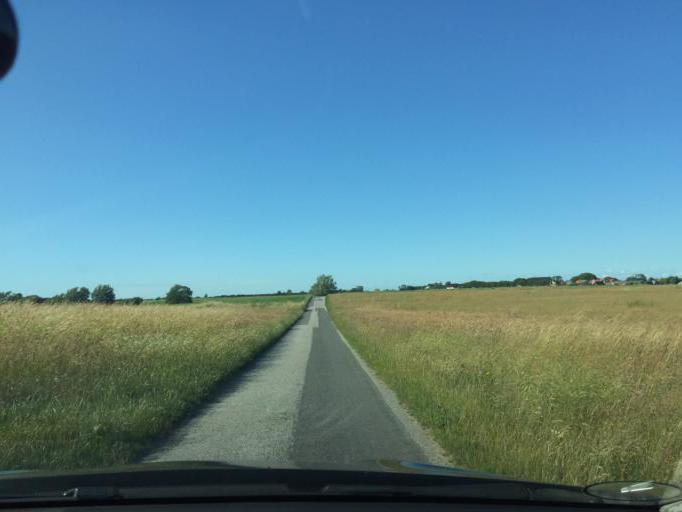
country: DK
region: Zealand
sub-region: Slagelse Kommune
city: Skaelskor
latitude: 55.2041
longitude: 11.1817
